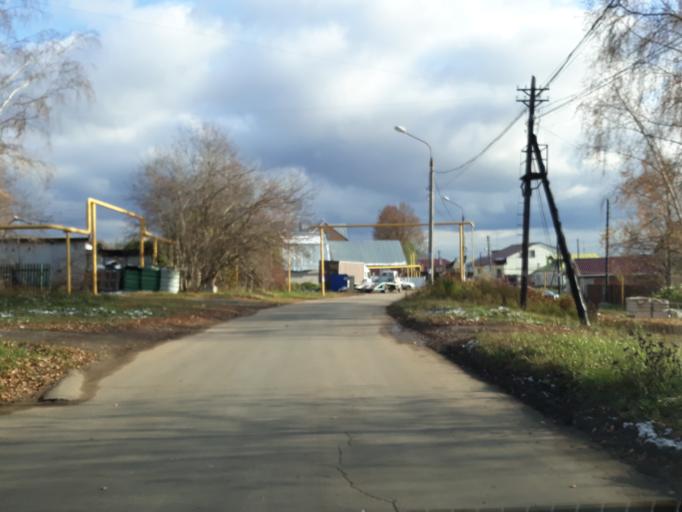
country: RU
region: Nizjnij Novgorod
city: Afonino
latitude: 56.2322
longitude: 44.0080
